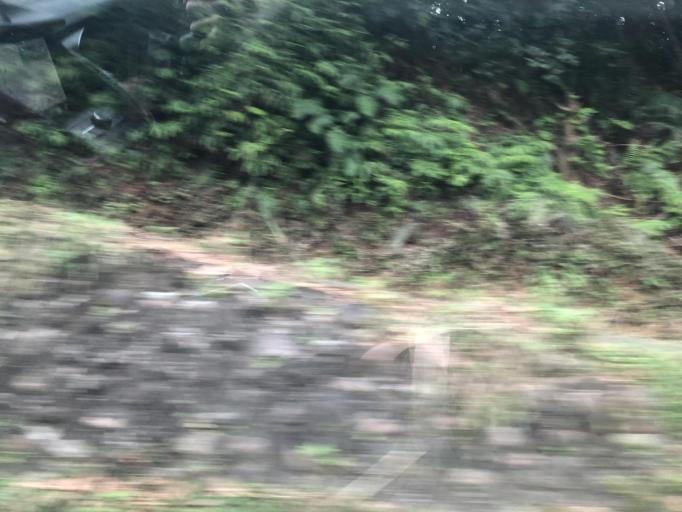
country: TW
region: Taiwan
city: Daxi
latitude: 24.9146
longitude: 121.3452
